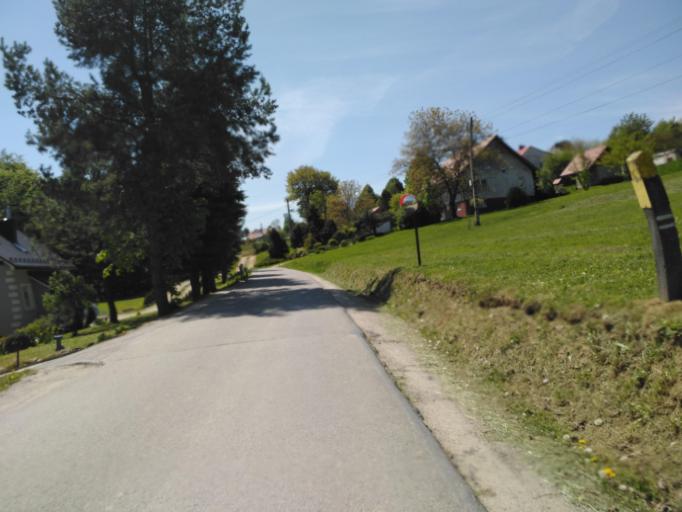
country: PL
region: Subcarpathian Voivodeship
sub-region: Powiat krosnienski
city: Iwonicz-Zdroj
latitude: 49.5487
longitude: 21.7778
